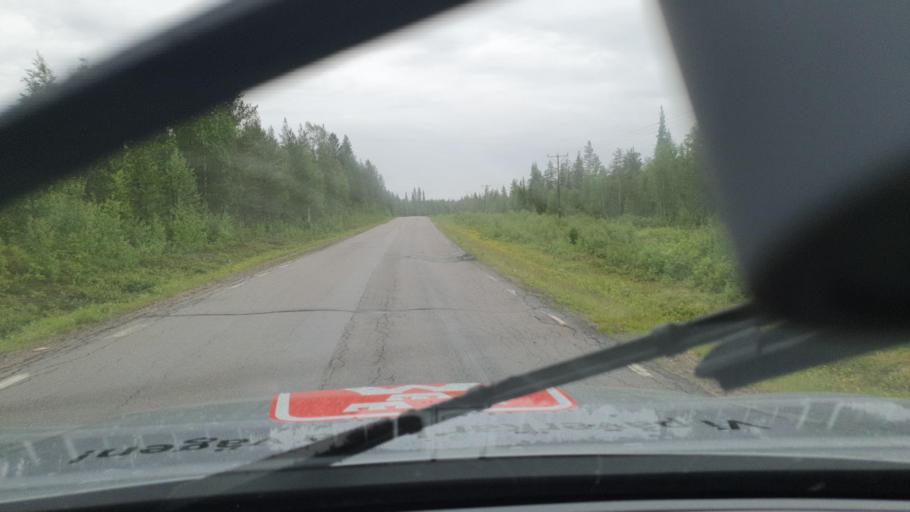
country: SE
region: Norrbotten
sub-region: Pajala Kommun
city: Pajala
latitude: 66.7801
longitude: 23.1382
